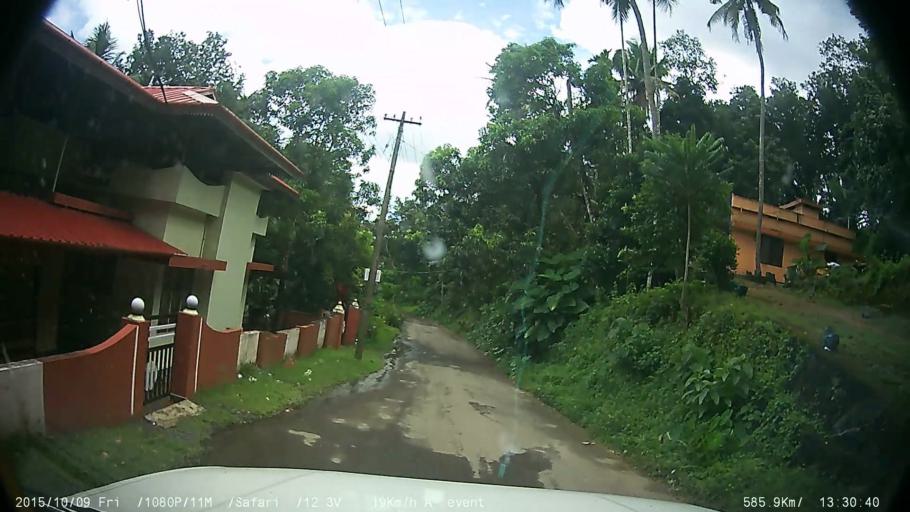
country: IN
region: Kerala
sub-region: Ernakulam
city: Ramamangalam
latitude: 9.9148
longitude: 76.5551
